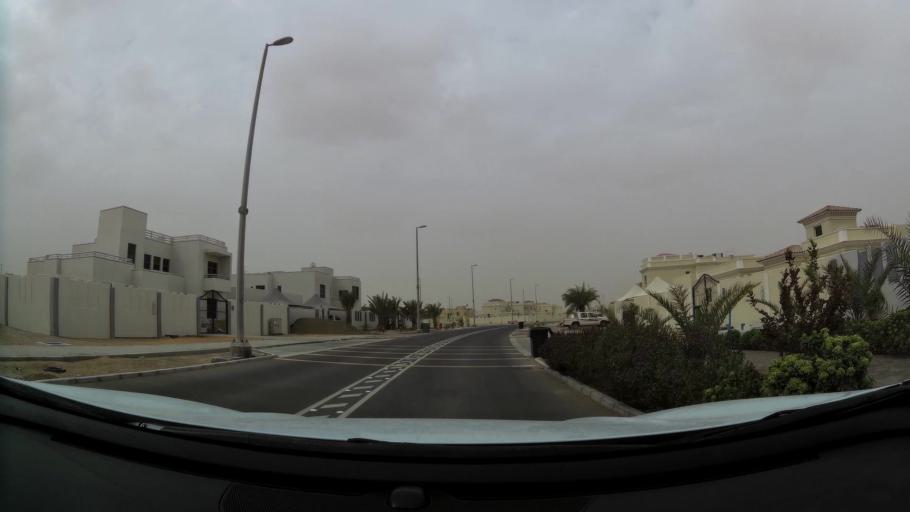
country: AE
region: Abu Dhabi
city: Abu Dhabi
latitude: 24.4413
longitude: 54.7387
